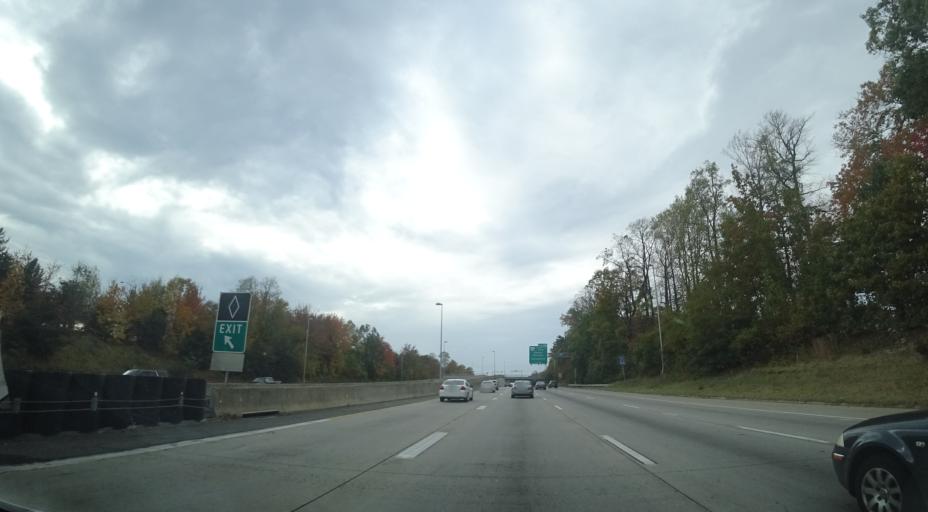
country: US
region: Virginia
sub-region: Fairfax County
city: Greenbriar
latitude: 38.8597
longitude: -77.3601
